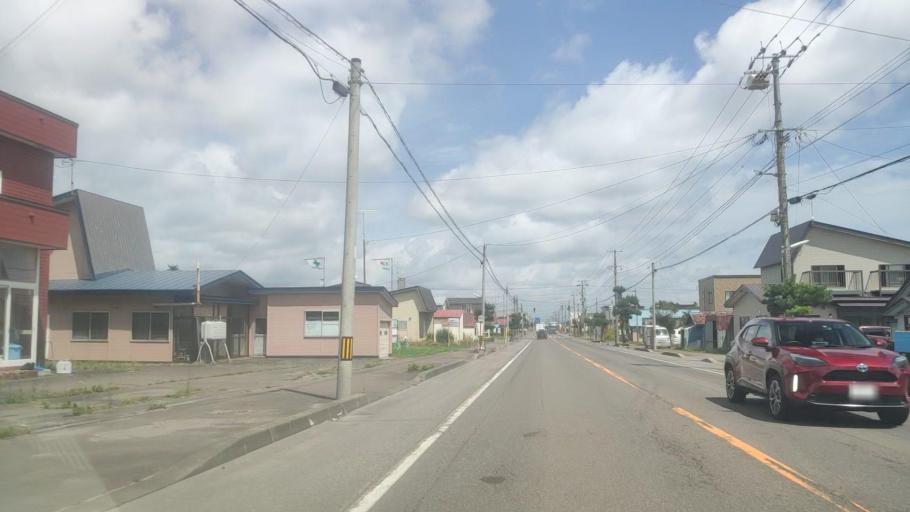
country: JP
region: Hokkaido
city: Niseko Town
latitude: 42.4350
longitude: 140.3208
